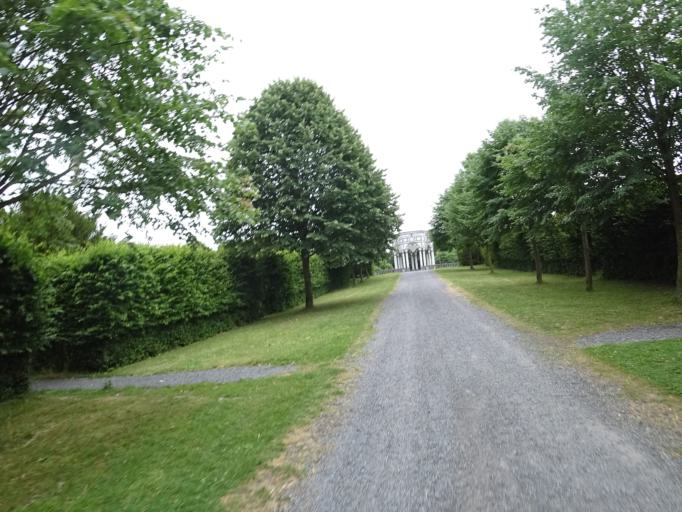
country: BE
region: Wallonia
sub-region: Province du Hainaut
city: Enghien
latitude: 50.6881
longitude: 4.0466
